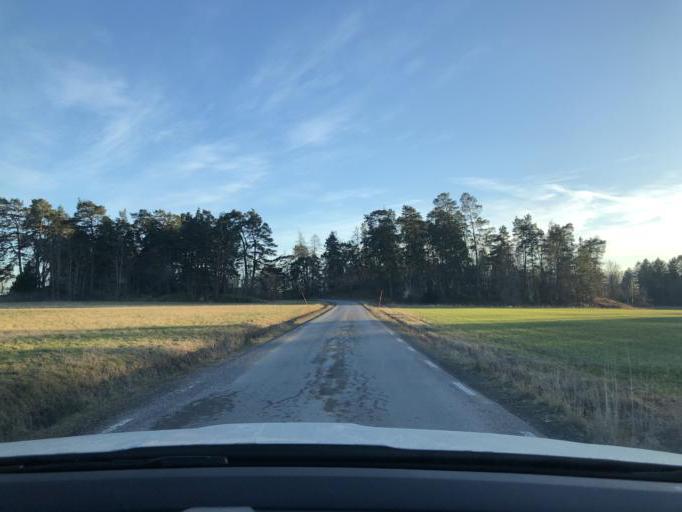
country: SE
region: Soedermanland
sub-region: Eskilstuna Kommun
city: Arla
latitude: 59.4128
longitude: 16.6920
